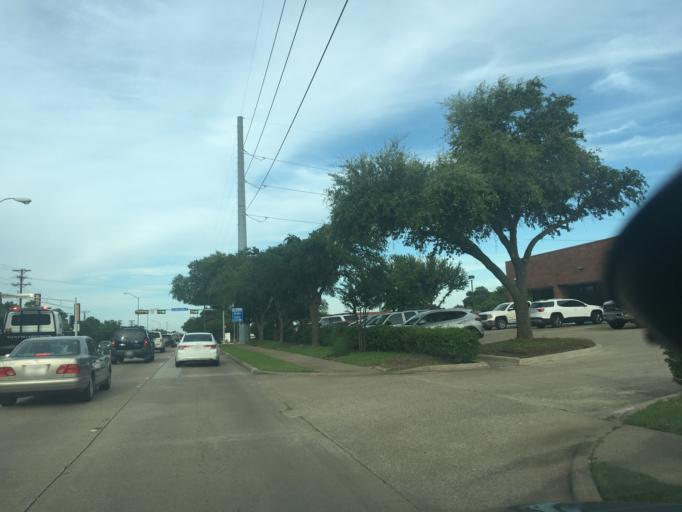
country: US
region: Texas
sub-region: Dallas County
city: Richardson
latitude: 32.9606
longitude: -96.7062
